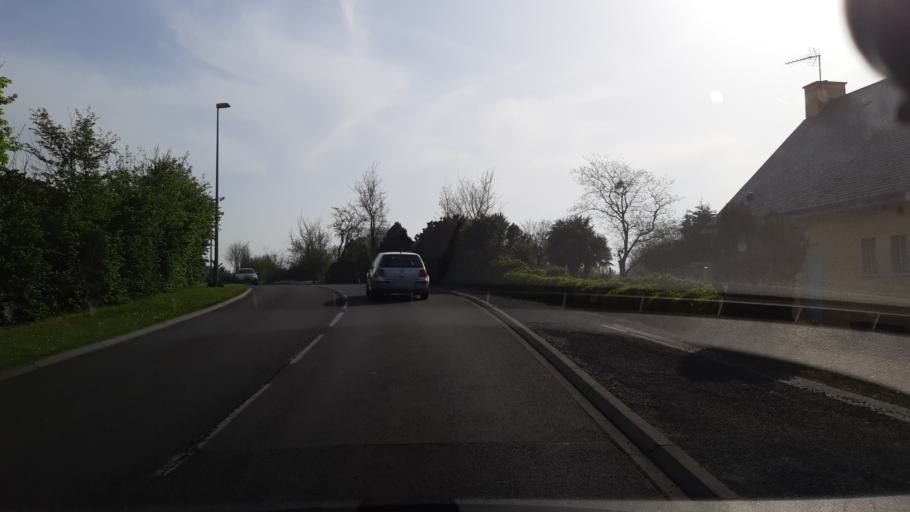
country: FR
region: Lower Normandy
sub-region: Departement de la Manche
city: Donville-les-Bains
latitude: 48.8613
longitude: -1.5551
